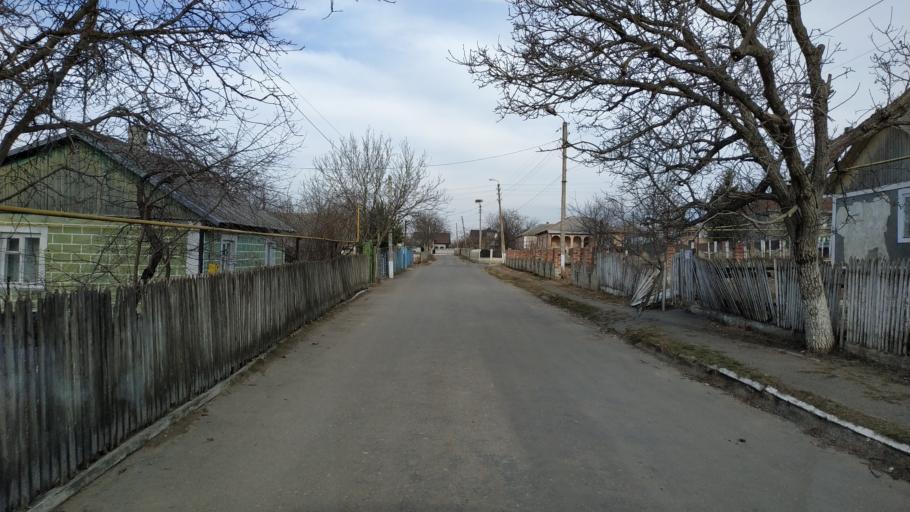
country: MD
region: Chisinau
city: Vatra
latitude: 46.9850
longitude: 28.6711
